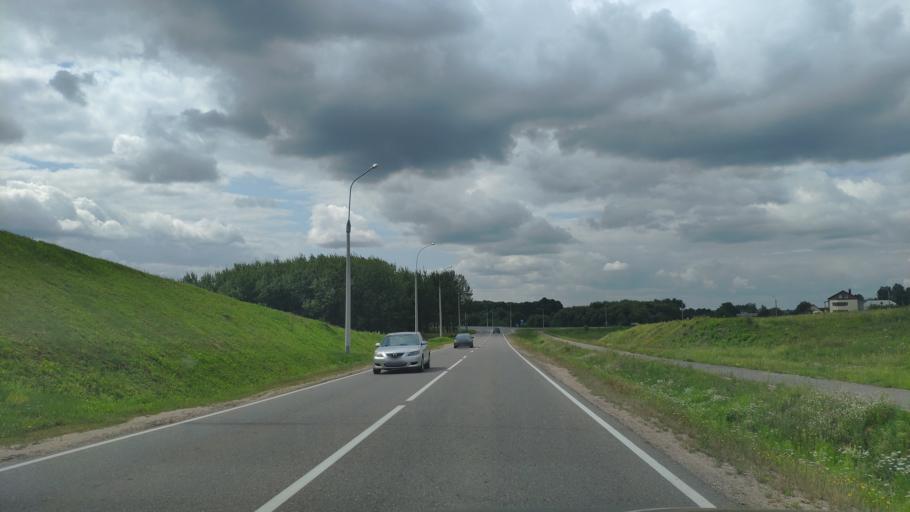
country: BY
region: Minsk
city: Zaslawye
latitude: 54.0063
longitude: 27.3077
